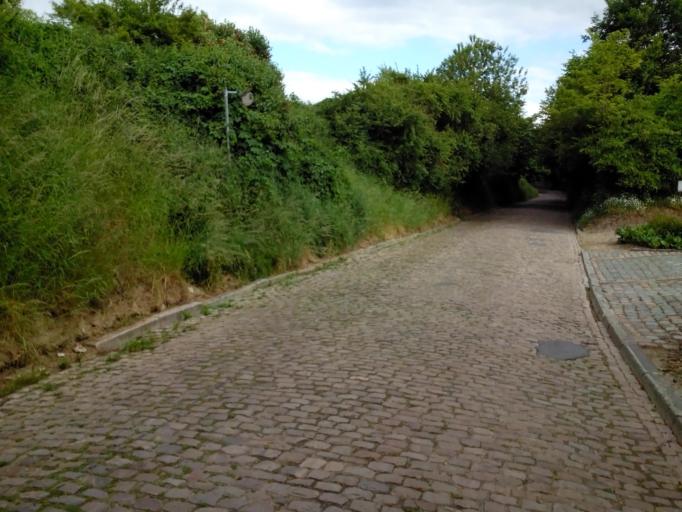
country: BE
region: Flanders
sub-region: Provincie Vlaams-Brabant
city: Leuven
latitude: 50.8621
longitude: 4.7294
